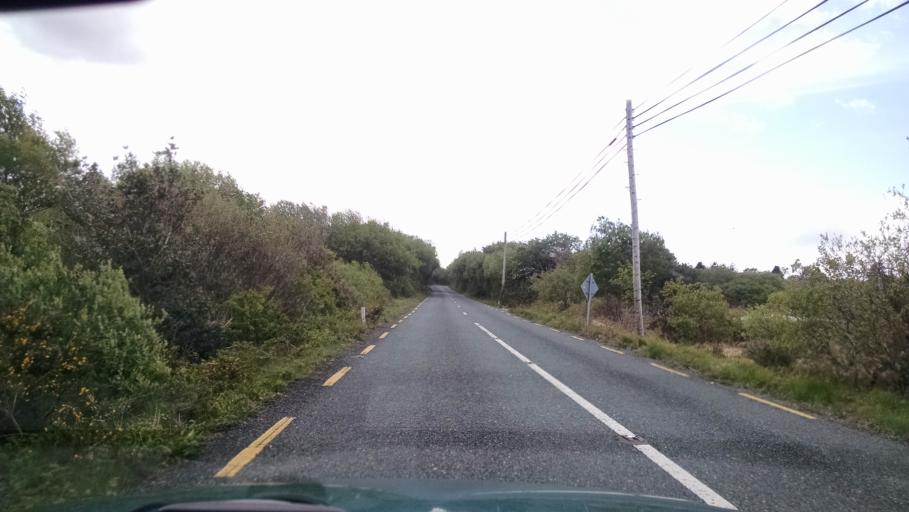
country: IE
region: Connaught
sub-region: County Galway
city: Oughterard
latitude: 53.3838
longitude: -9.5787
